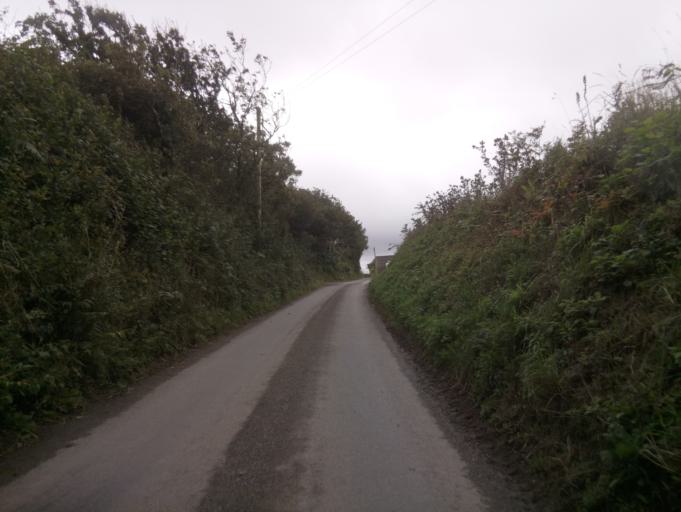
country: GB
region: England
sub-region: Devon
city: Kingsbridge
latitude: 50.3102
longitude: -3.7160
